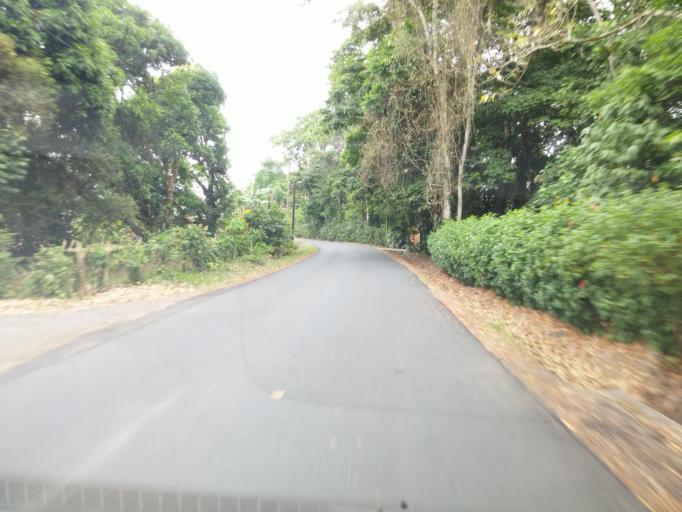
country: CR
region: Alajuela
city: Quesada
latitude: 10.3351
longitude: -84.5154
